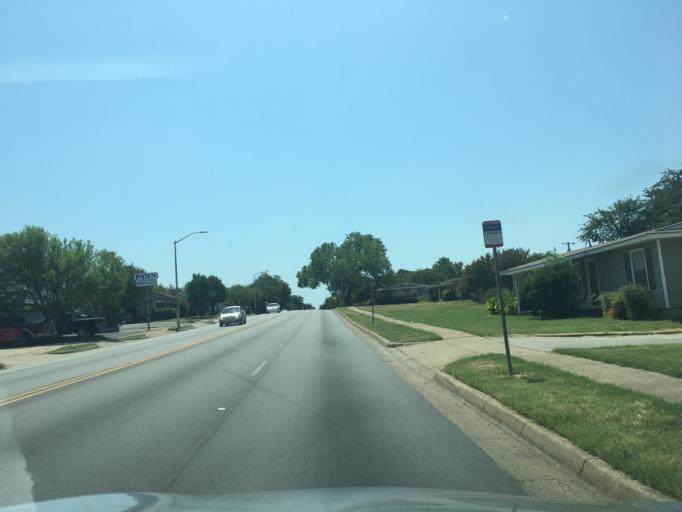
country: US
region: Texas
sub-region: Tarrant County
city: Edgecliff Village
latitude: 32.6893
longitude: -97.3531
